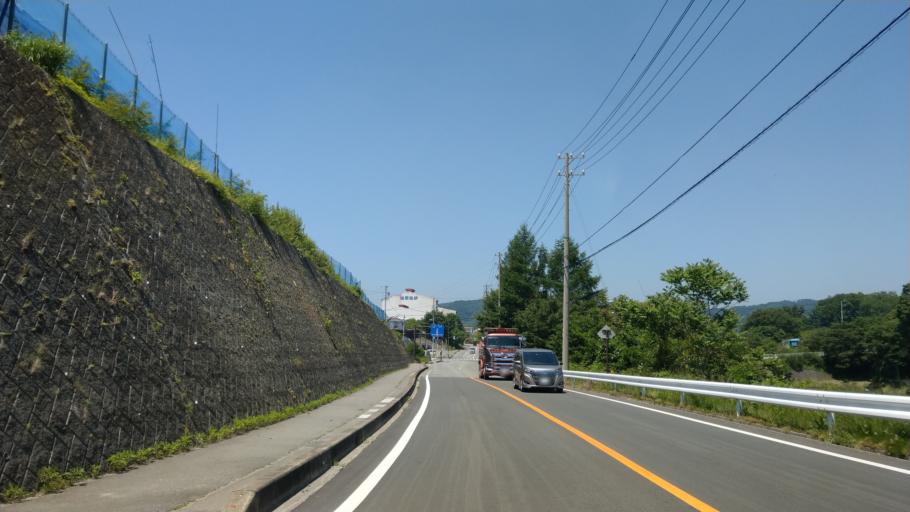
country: JP
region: Nagano
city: Komoro
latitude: 36.2937
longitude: 138.4421
